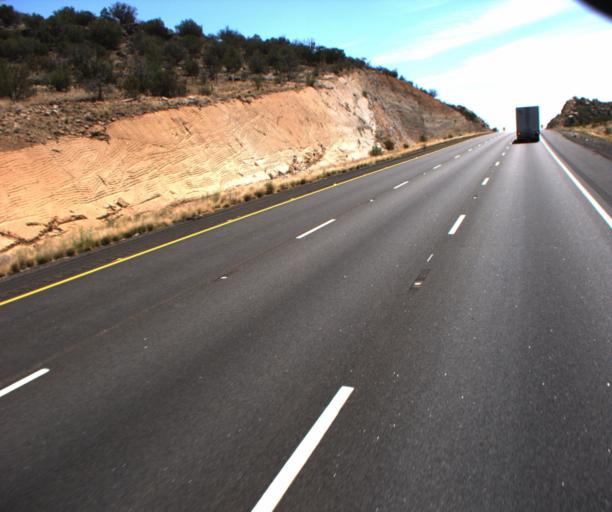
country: US
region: Arizona
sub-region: Mohave County
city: Peach Springs
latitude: 35.1861
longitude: -113.4090
